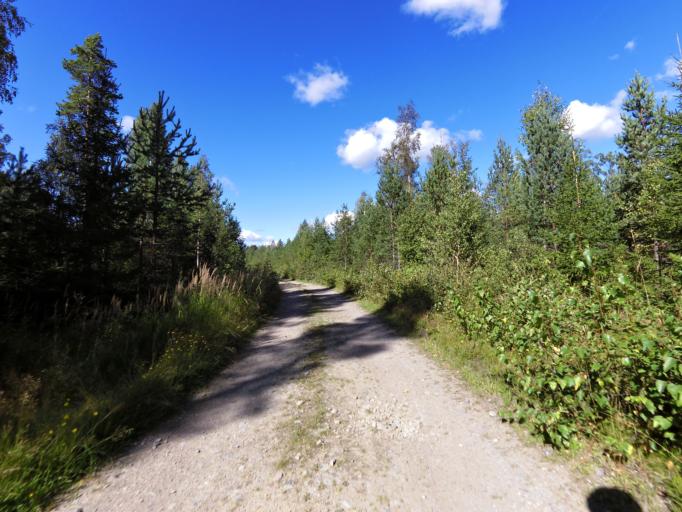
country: SE
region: Gaevleborg
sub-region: Gavle Kommun
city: Valbo
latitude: 60.7496
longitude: 16.9798
